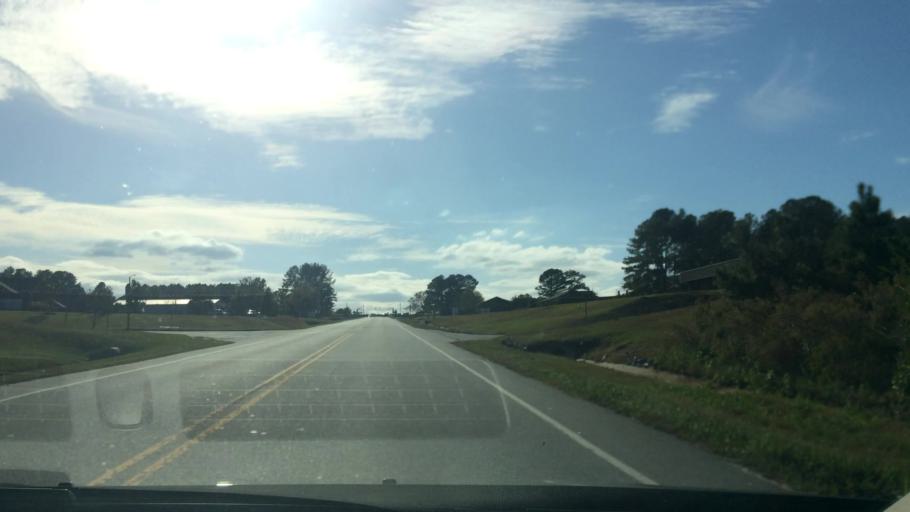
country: US
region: North Carolina
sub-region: Greene County
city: Snow Hill
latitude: 35.4553
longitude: -77.6809
